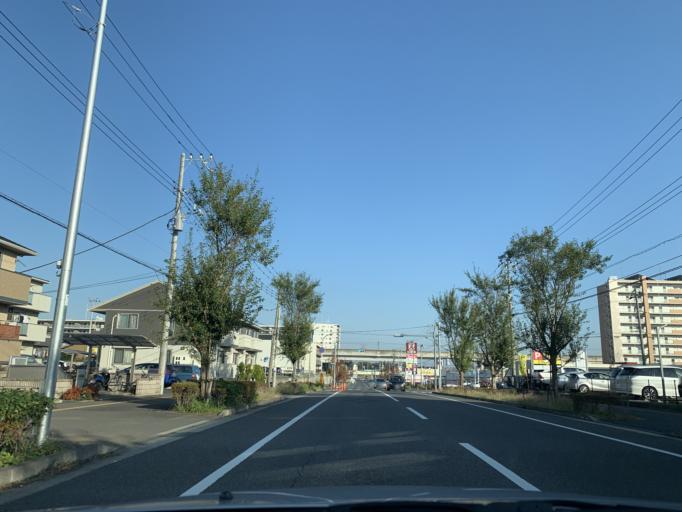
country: JP
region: Ibaraki
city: Moriya
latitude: 35.9131
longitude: 139.9552
